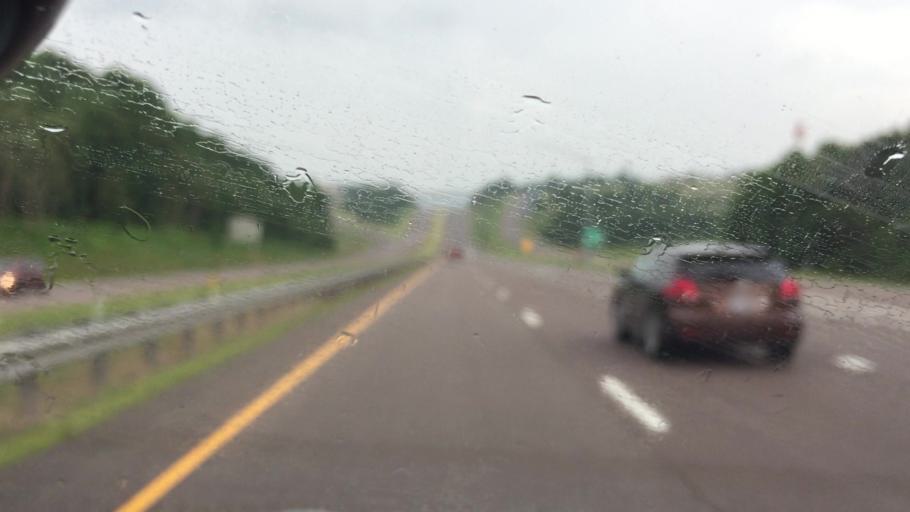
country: US
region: Pennsylvania
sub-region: Somerset County
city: Meyersdale
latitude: 39.6870
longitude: -79.0947
